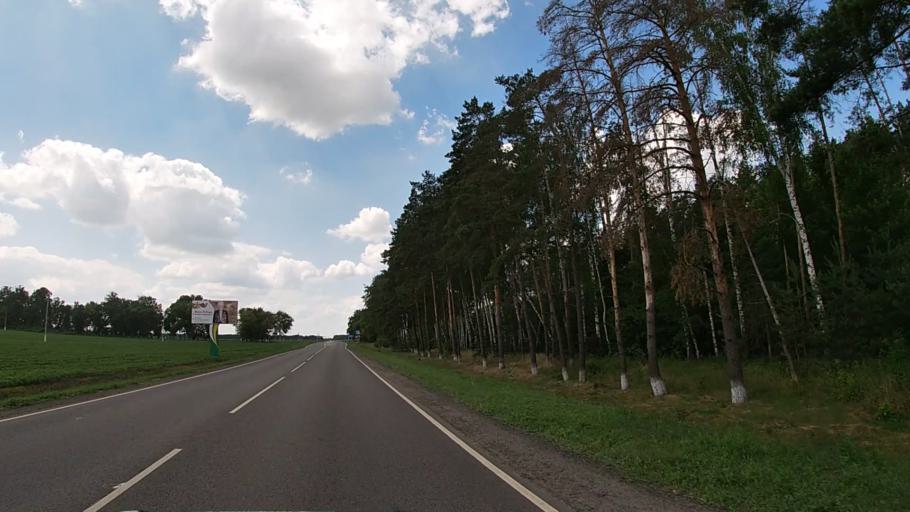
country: RU
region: Belgorod
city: Golovchino
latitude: 50.5066
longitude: 35.7440
